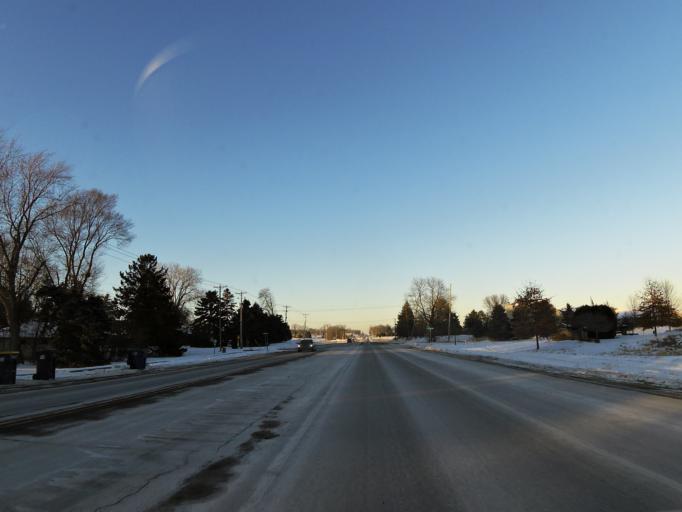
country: US
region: Minnesota
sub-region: Dakota County
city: Farmington
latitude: 44.6678
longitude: -93.1366
